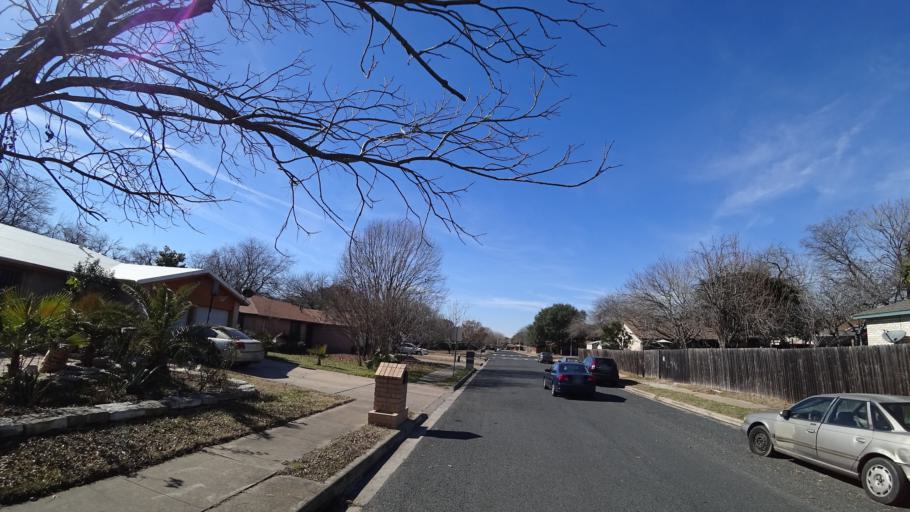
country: US
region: Texas
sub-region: Travis County
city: Wells Branch
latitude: 30.3817
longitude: -97.6972
